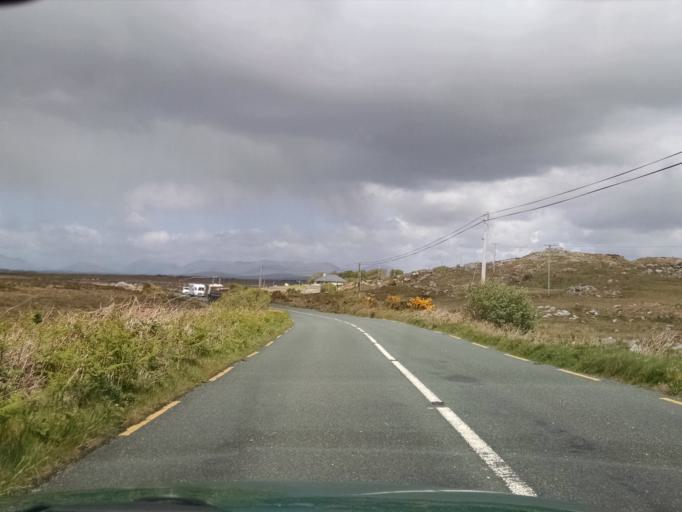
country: IE
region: Connaught
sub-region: County Galway
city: Oughterard
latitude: 53.3004
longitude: -9.5541
